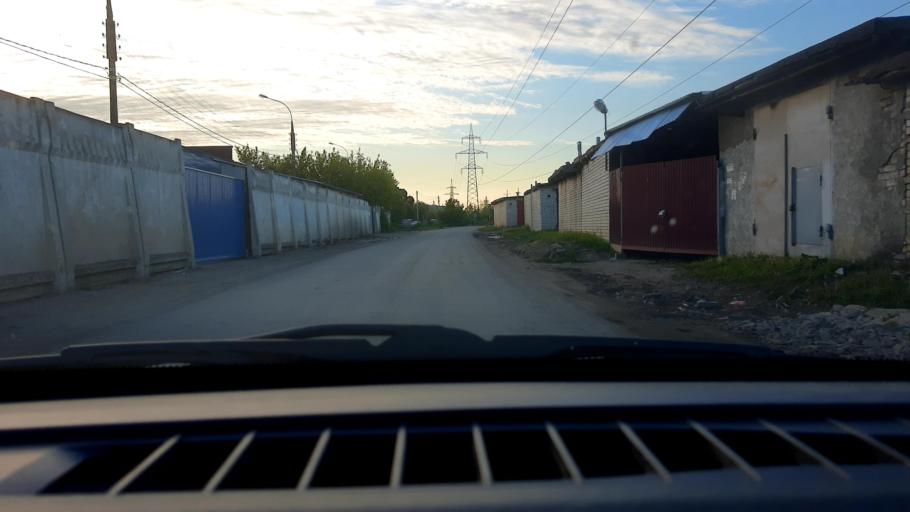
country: RU
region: Nizjnij Novgorod
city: Nizhniy Novgorod
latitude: 56.2758
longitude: 43.8954
